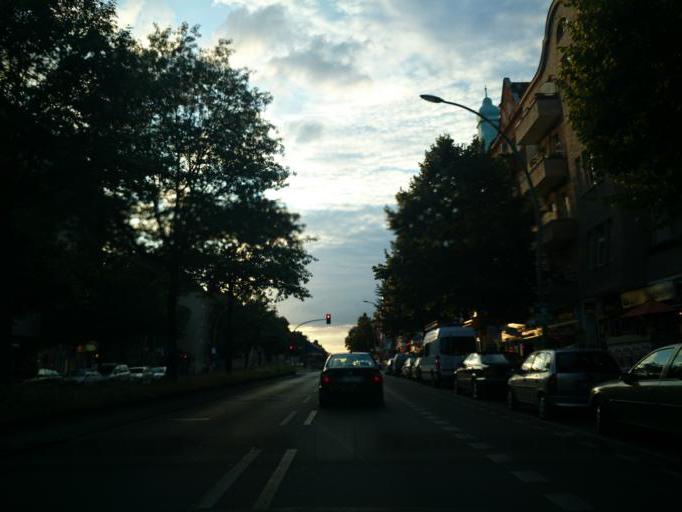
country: DE
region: Berlin
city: Reinickendorf
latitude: 52.5557
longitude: 13.3431
